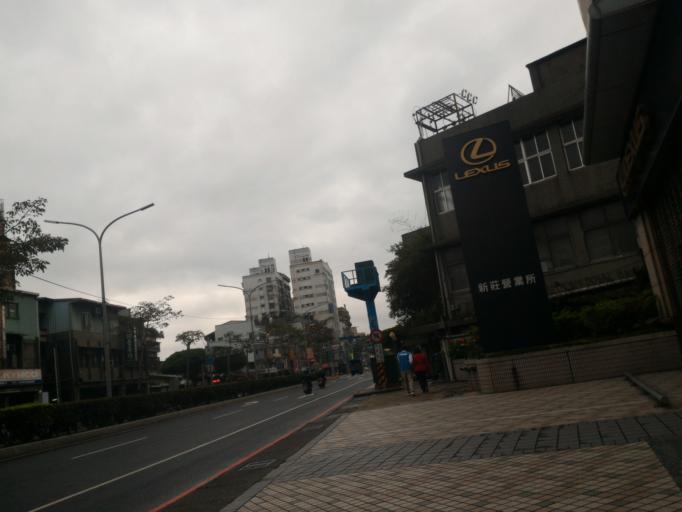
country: TW
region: Taipei
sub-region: Taipei
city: Banqiao
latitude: 25.0388
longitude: 121.4600
